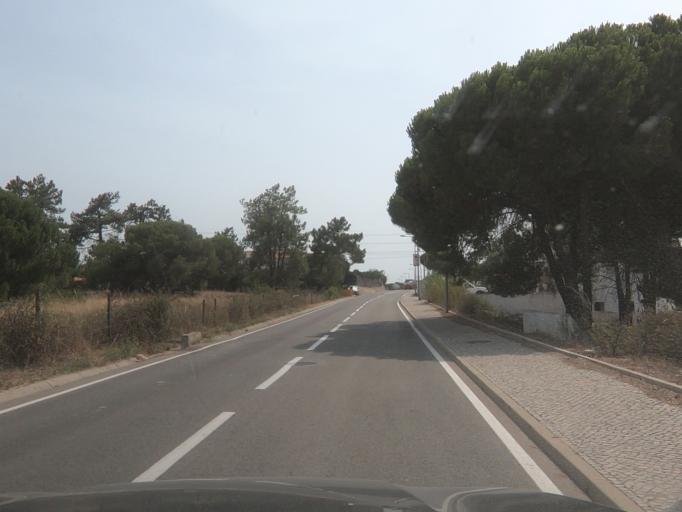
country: PT
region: Faro
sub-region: Loule
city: Quarteira
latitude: 37.0847
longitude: -8.0750
